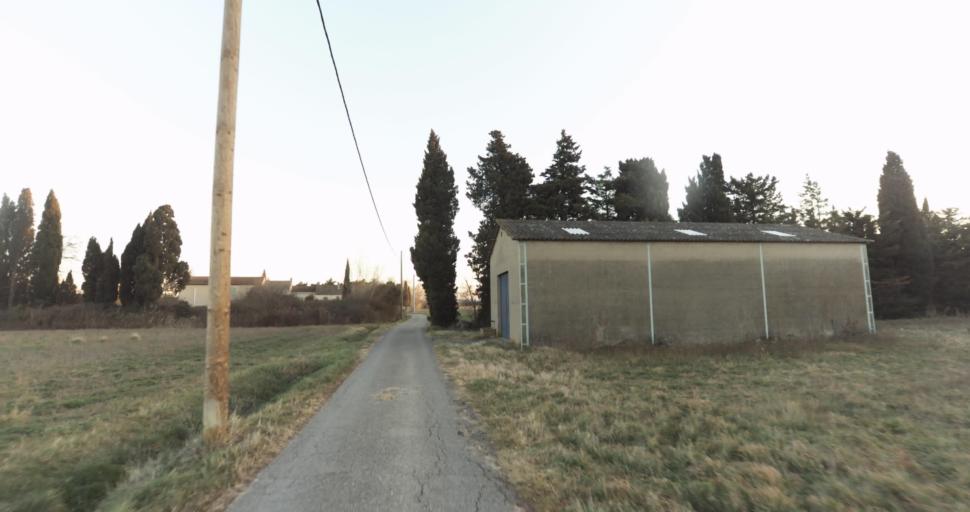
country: FR
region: Provence-Alpes-Cote d'Azur
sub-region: Departement des Bouches-du-Rhone
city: Barbentane
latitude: 43.8902
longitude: 4.7764
